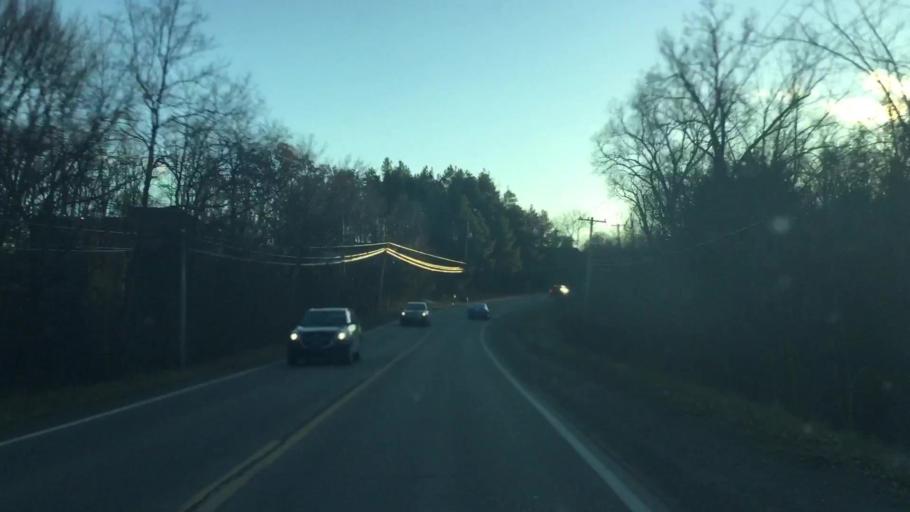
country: US
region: Michigan
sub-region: Genesee County
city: Argentine
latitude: 42.8008
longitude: -83.8225
